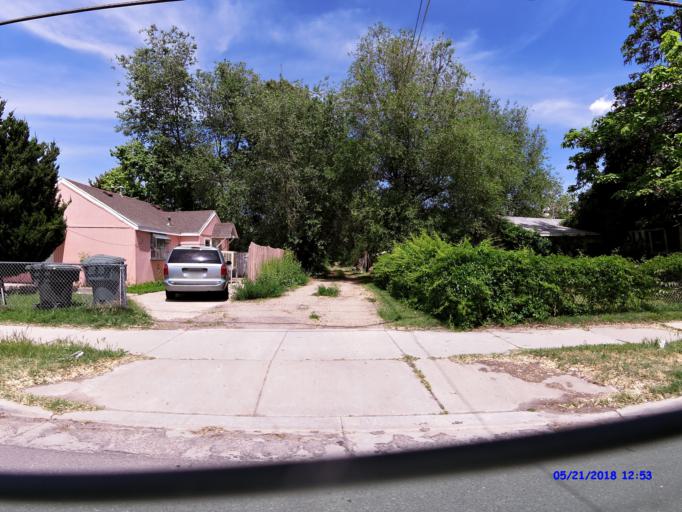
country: US
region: Utah
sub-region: Weber County
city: South Ogden
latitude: 41.1977
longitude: -111.9661
